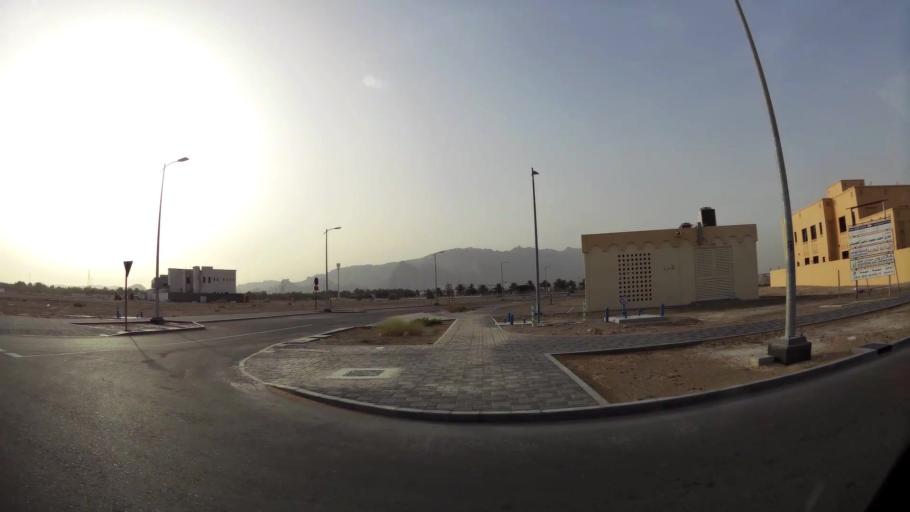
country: AE
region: Abu Dhabi
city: Al Ain
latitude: 24.1068
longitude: 55.7135
